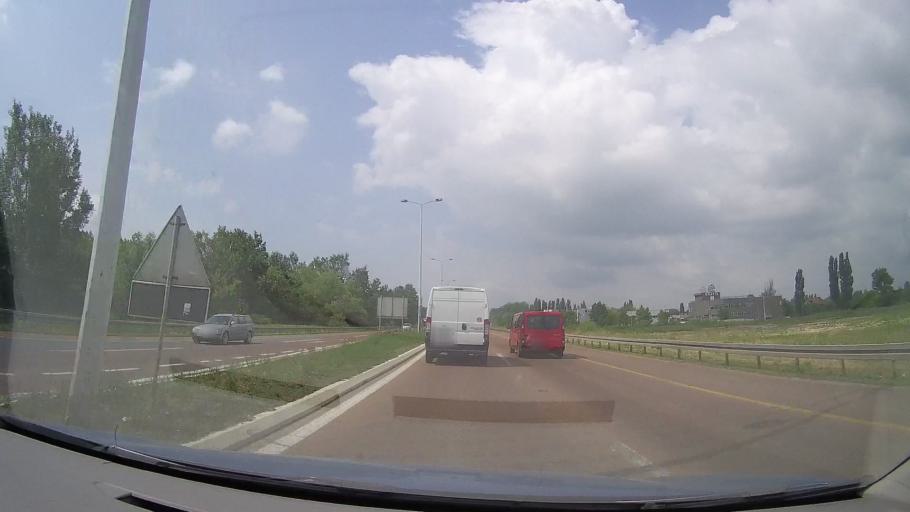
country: RS
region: Central Serbia
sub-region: Belgrade
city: Palilula
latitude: 44.8433
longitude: 20.5078
